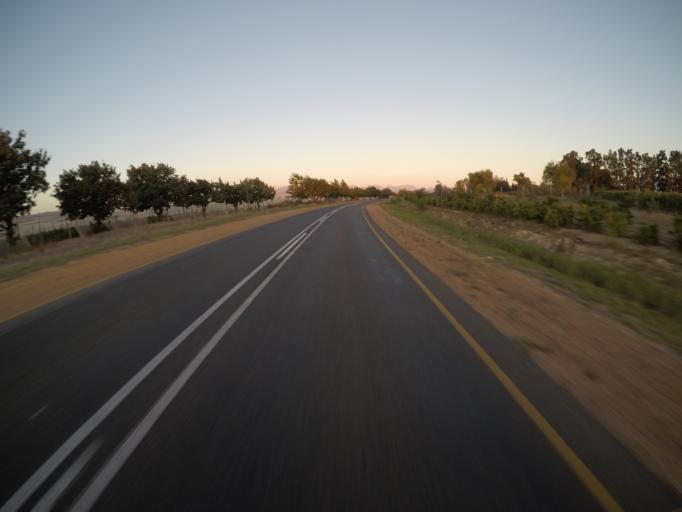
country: ZA
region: Western Cape
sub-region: Cape Winelands District Municipality
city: Paarl
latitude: -33.8032
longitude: 18.8899
